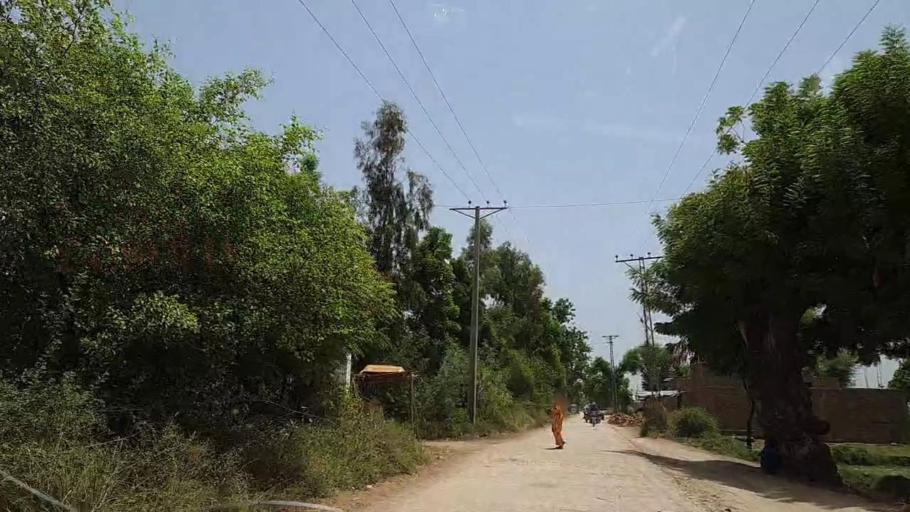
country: PK
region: Sindh
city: Tharu Shah
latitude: 26.9467
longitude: 68.1056
